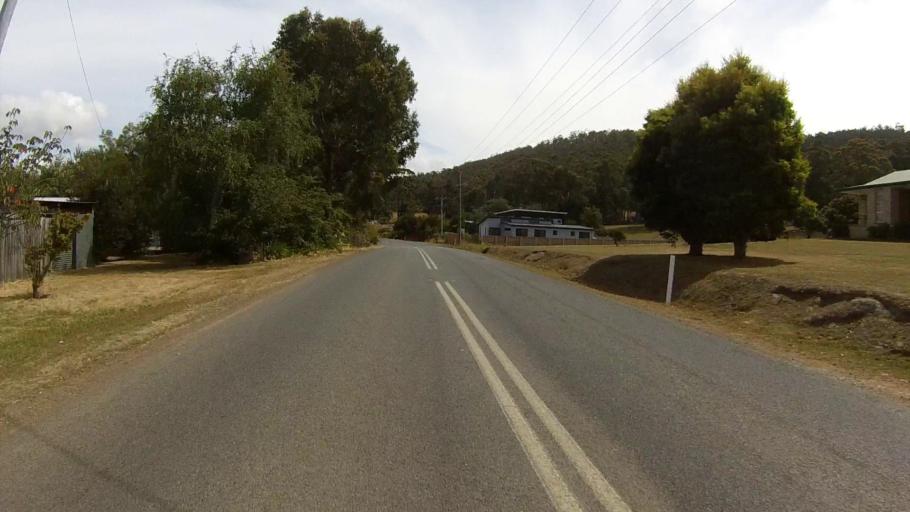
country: AU
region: Tasmania
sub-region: Huon Valley
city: Cygnet
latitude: -43.2083
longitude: 147.1153
